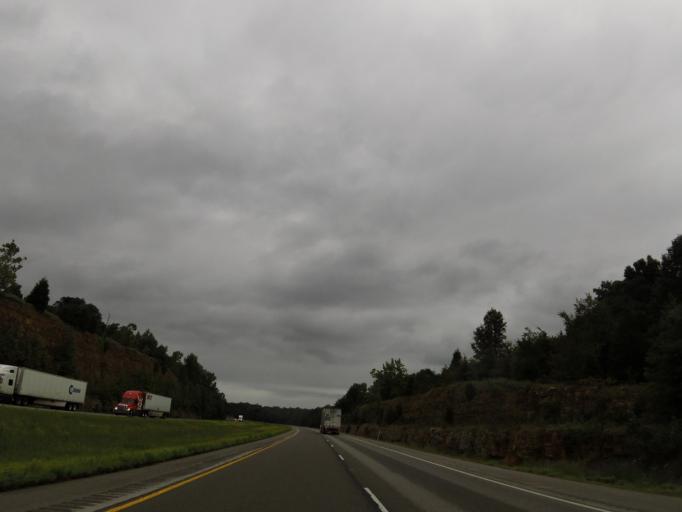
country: US
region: Illinois
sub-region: Massac County
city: Metropolis
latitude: 37.3150
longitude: -88.7580
